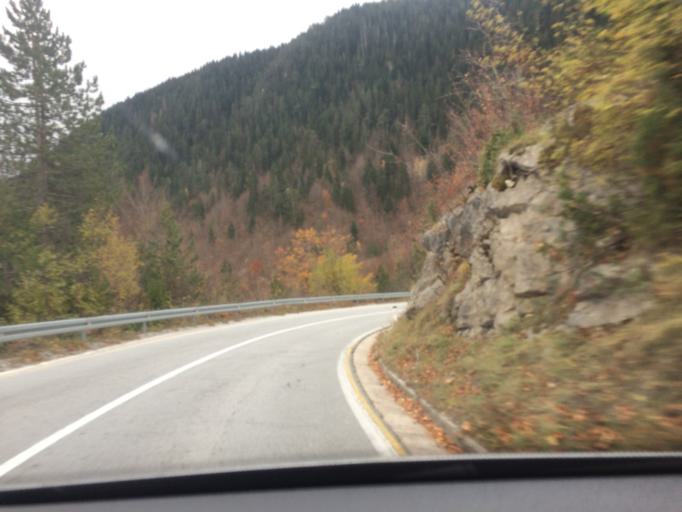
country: ME
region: Opstina Zabljak
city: Zabljak
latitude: 43.1490
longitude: 19.2685
